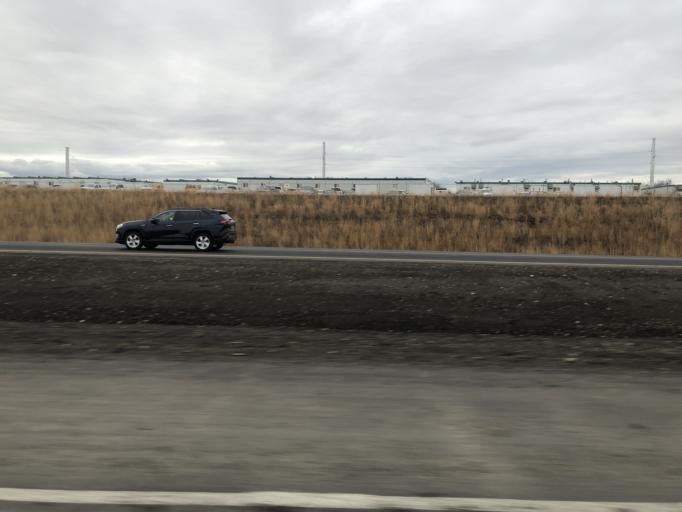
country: CA
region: Alberta
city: Calgary
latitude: 50.9543
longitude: -114.1423
